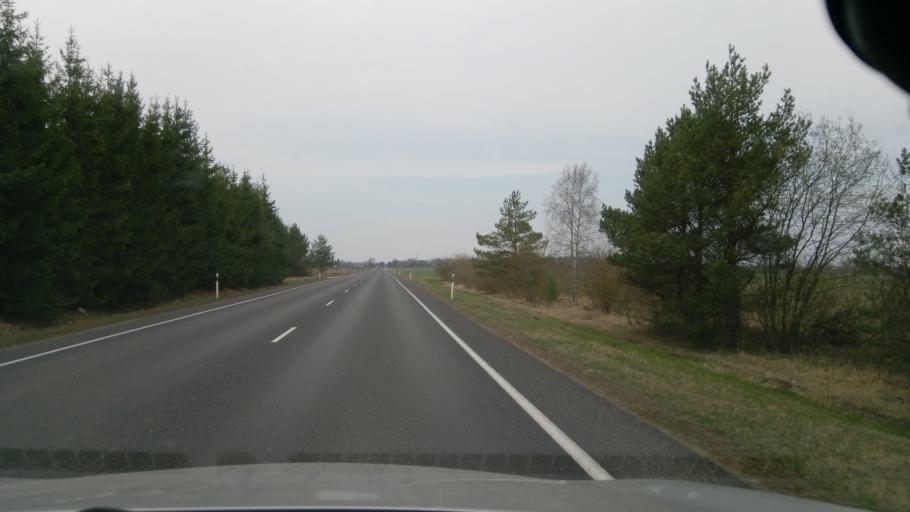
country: EE
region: Viljandimaa
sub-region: Vohma linn
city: Vohma
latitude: 58.7445
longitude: 25.5768
